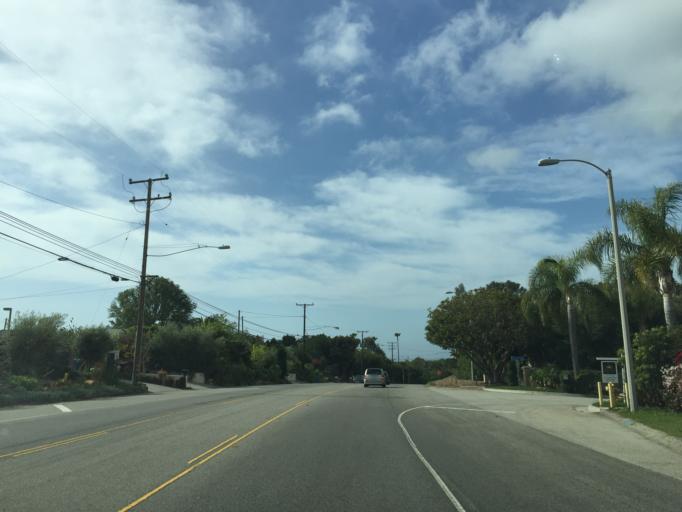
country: US
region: California
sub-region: Los Angeles County
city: Malibu
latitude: 34.0305
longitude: -118.7976
